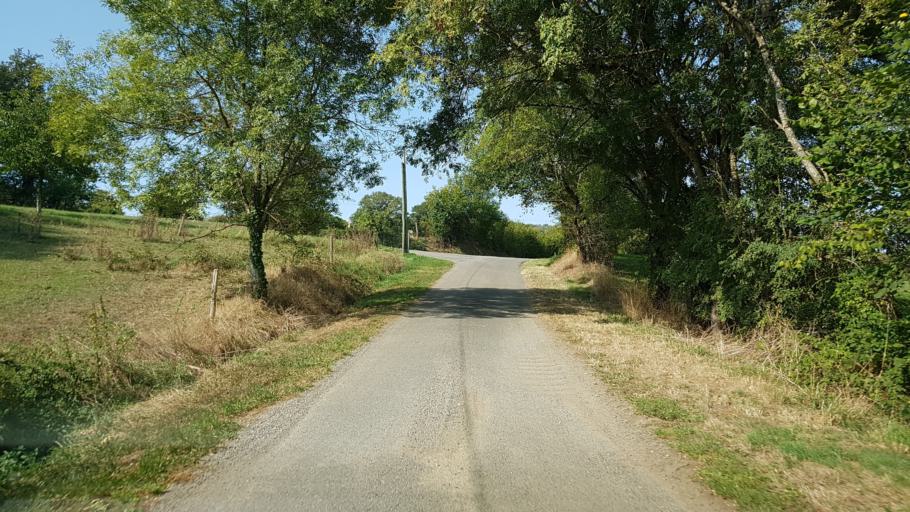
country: FR
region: Poitou-Charentes
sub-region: Departement de la Charente
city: Etagnac
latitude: 45.9226
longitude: 0.7829
